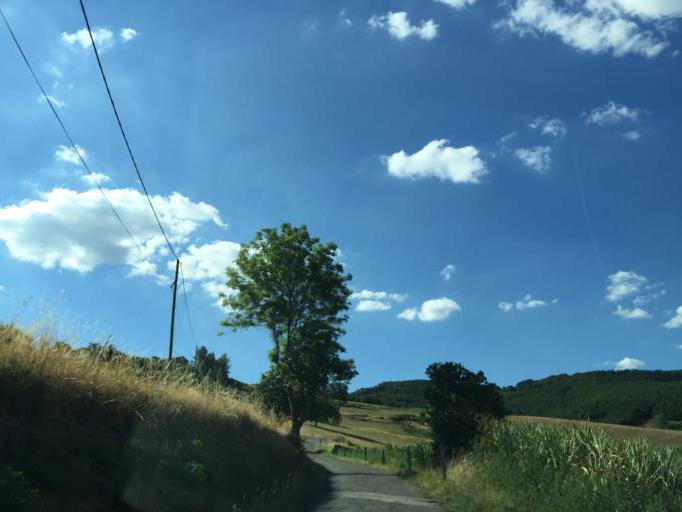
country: FR
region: Rhone-Alpes
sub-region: Departement de la Loire
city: Saint-Chamond
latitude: 45.5031
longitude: 4.4979
